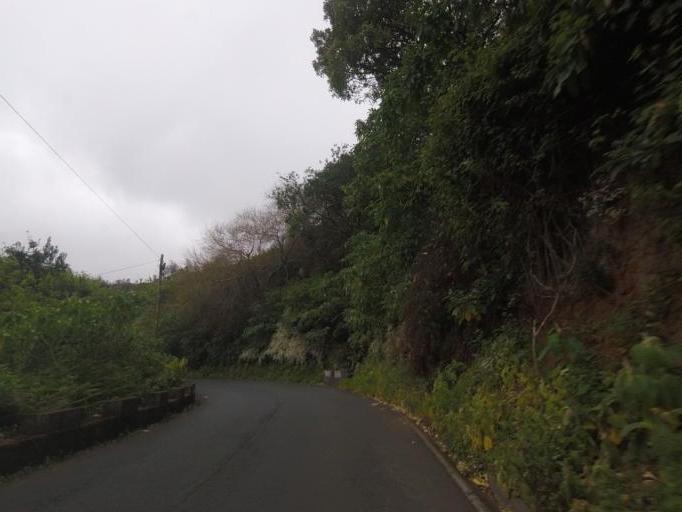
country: PT
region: Madeira
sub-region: Santa Cruz
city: Santa Cruz
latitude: 32.7360
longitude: -16.8152
